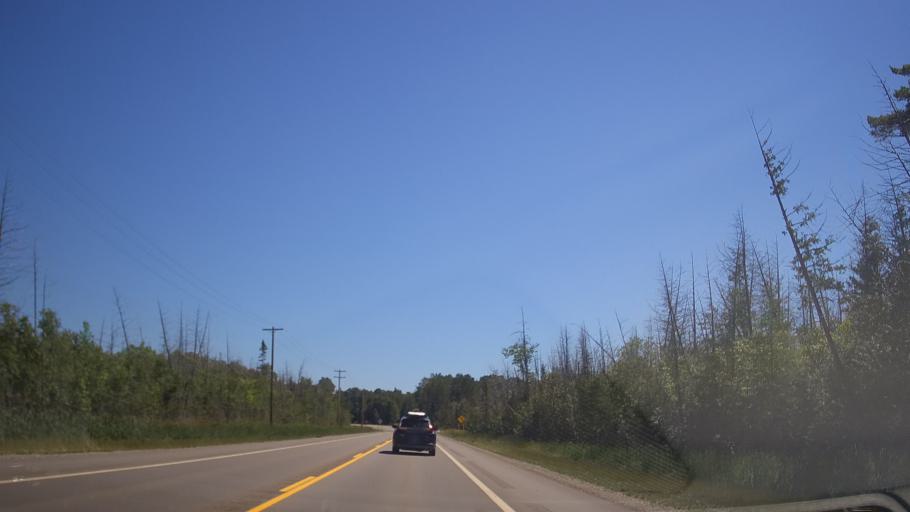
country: US
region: Michigan
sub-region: Mackinac County
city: Saint Ignace
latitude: 45.6251
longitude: -84.7822
